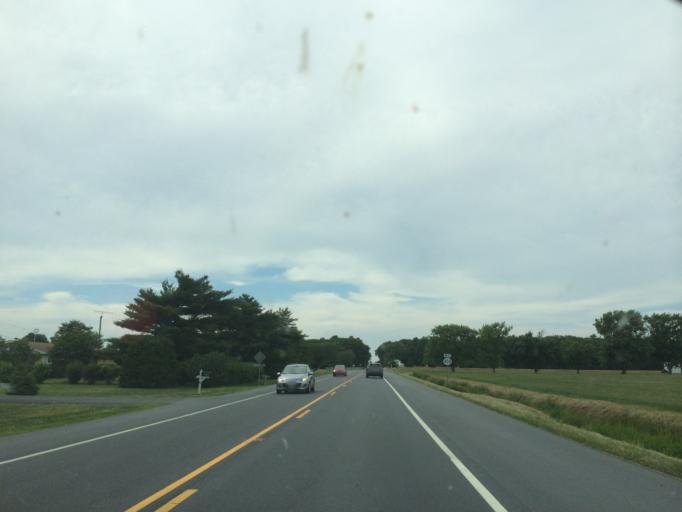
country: US
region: Delaware
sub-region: Sussex County
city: Bridgeville
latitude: 38.7578
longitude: -75.6344
